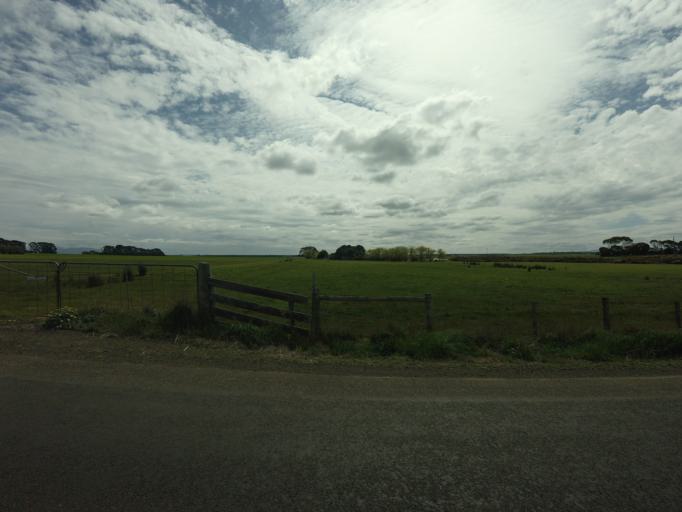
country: AU
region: Tasmania
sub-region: Northern Midlands
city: Longford
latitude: -41.7154
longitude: 147.1902
